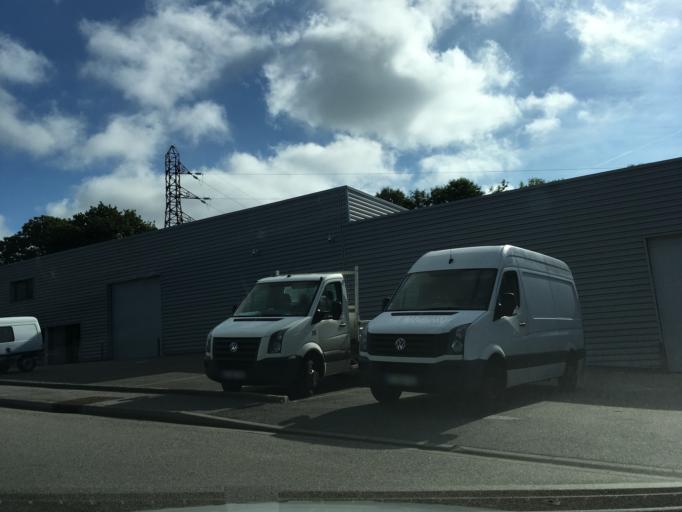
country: FR
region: Brittany
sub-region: Departement du Finistere
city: Quimper
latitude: 48.0079
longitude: -4.0726
